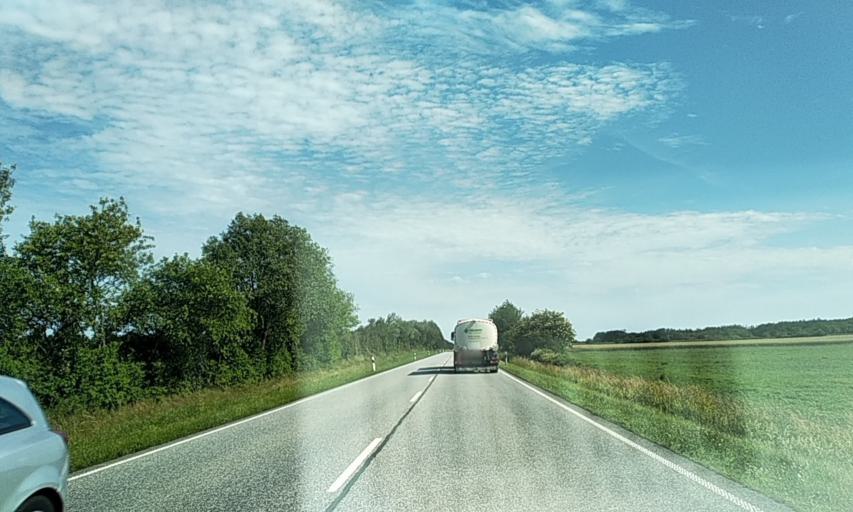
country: DE
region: Schleswig-Holstein
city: Kropp
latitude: 54.4246
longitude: 9.5311
